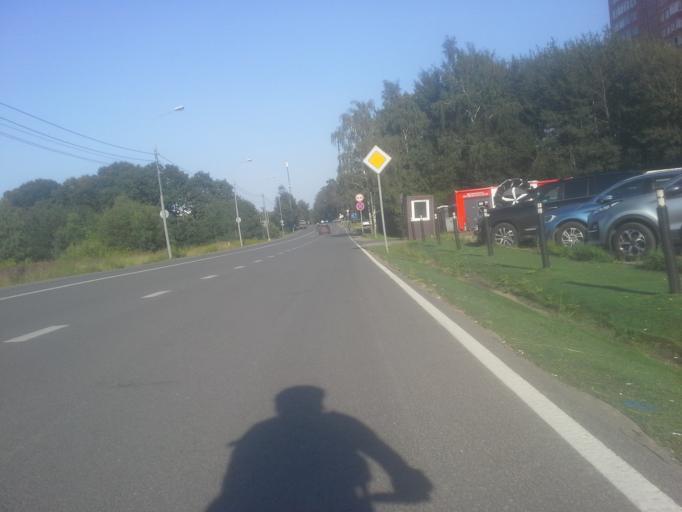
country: RU
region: Moskovskaya
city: Nikolina Gora
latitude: 55.7066
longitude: 37.0232
